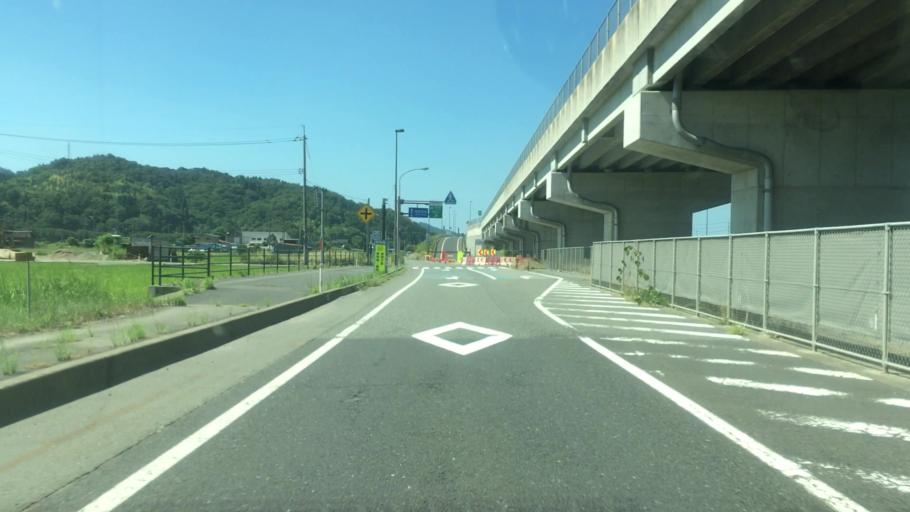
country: JP
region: Tottori
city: Tottori
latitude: 35.4297
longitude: 134.2061
